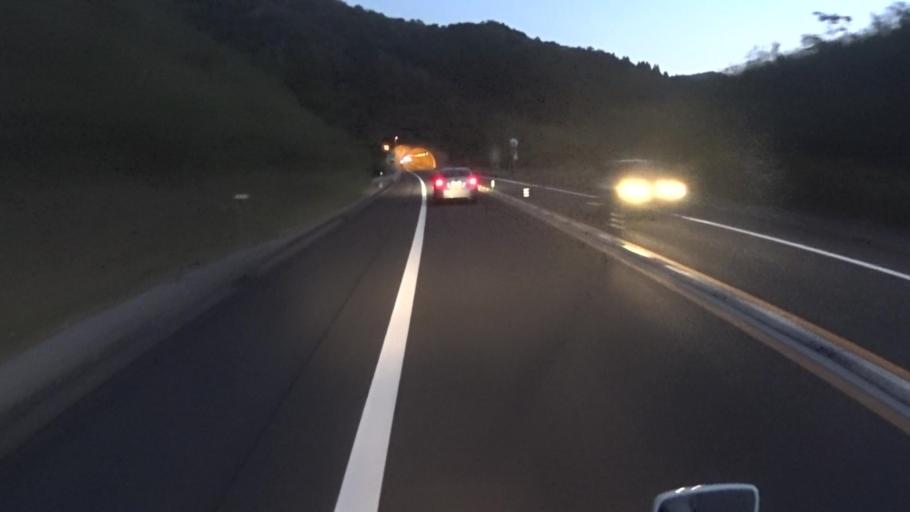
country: JP
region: Kyoto
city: Miyazu
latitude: 35.4632
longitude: 135.1737
